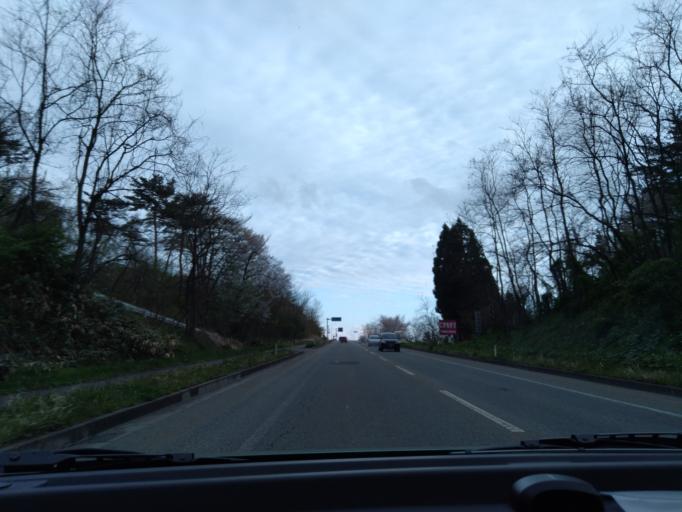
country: JP
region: Akita
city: Akita
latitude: 39.7399
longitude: 140.1367
